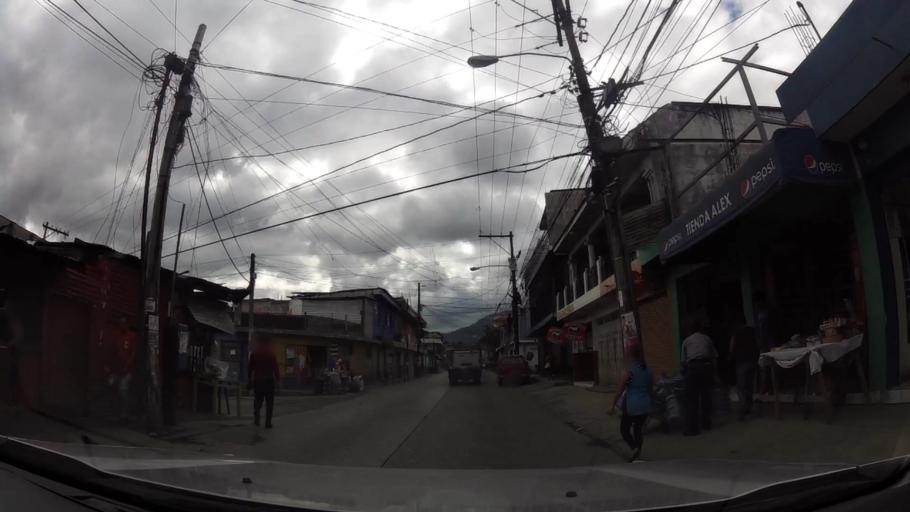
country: GT
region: Guatemala
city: Mixco
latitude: 14.6456
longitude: -90.5933
